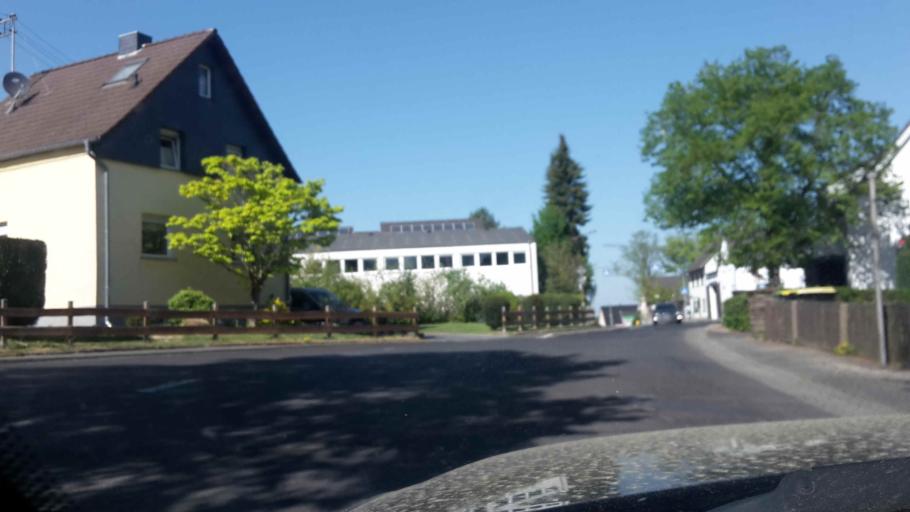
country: DE
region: Rheinland-Pfalz
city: Windhagen
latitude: 50.6863
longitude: 7.3356
